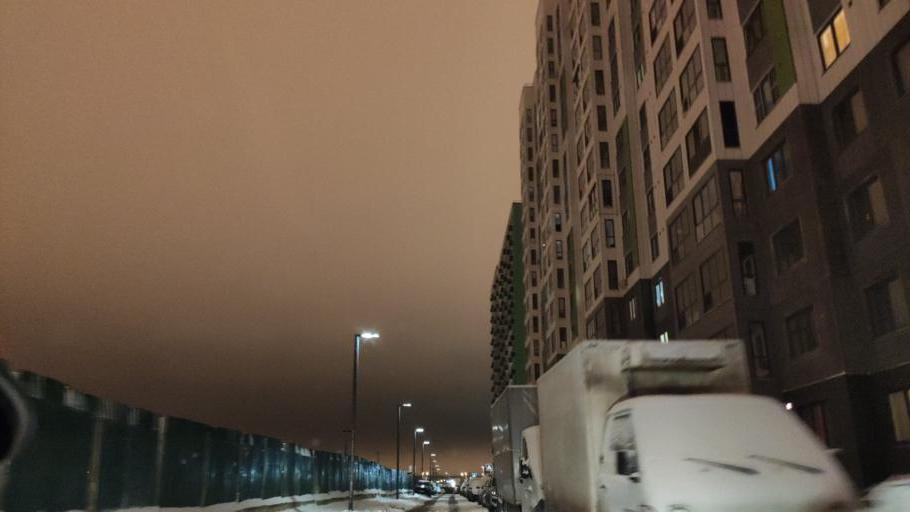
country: RU
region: Moskovskaya
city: Shcherbinka
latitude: 55.5238
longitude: 37.5890
